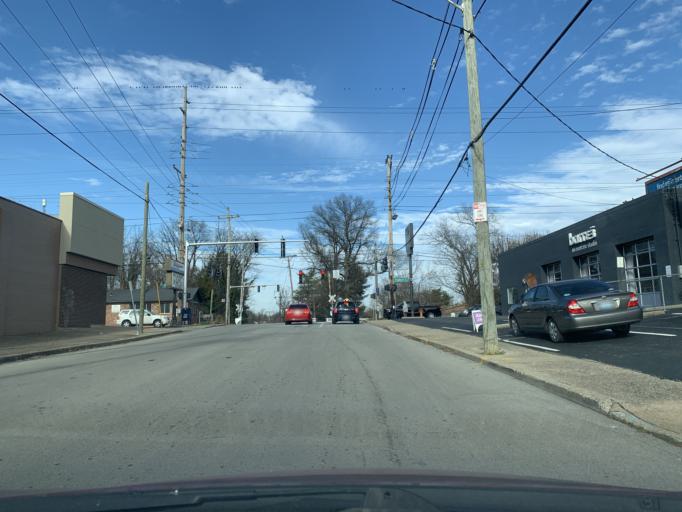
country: US
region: Kentucky
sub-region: Jefferson County
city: Indian Hills
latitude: 38.2533
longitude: -85.6998
